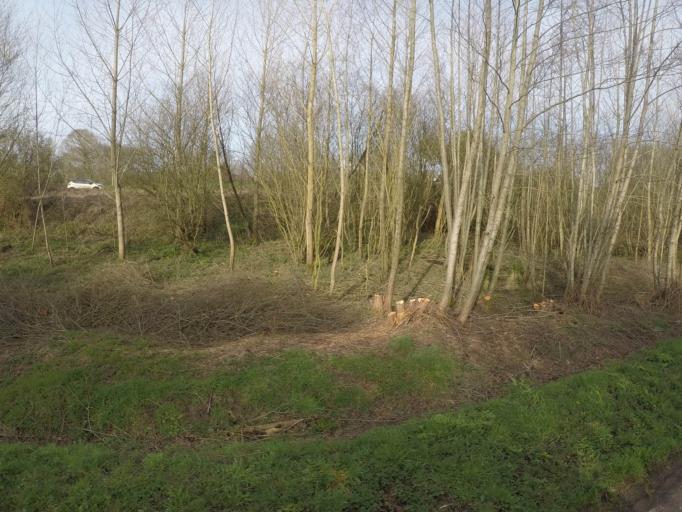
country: FR
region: Brittany
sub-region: Departement des Cotes-d'Armor
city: Plelo
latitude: 48.5266
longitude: -2.9657
